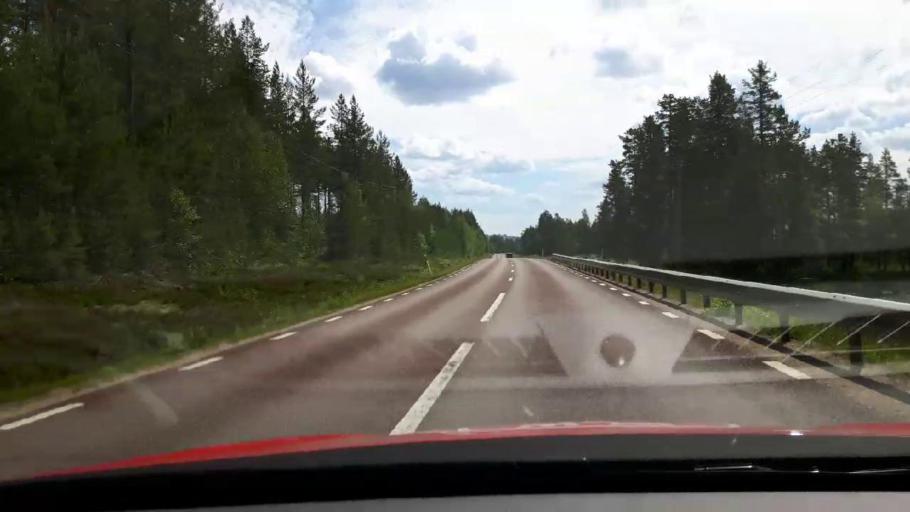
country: SE
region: Jaemtland
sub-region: Harjedalens Kommun
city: Sveg
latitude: 62.1424
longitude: 14.9586
